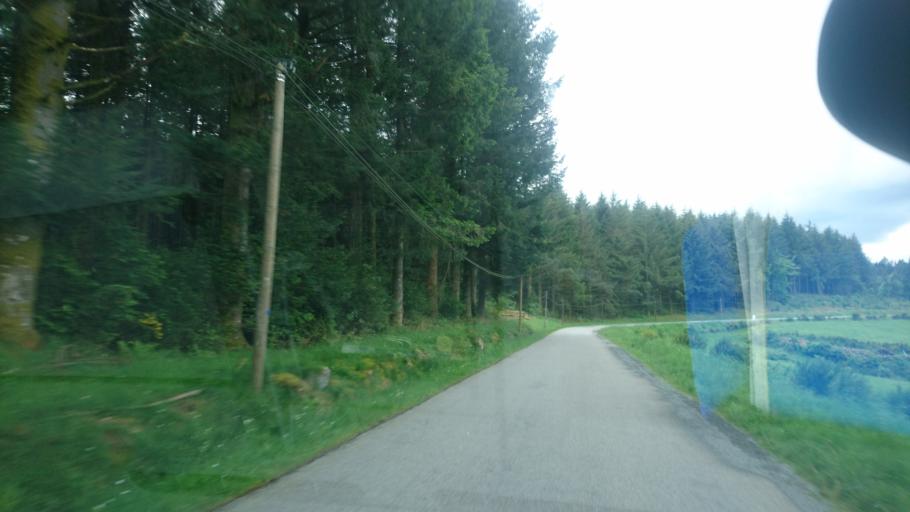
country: FR
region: Limousin
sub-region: Departement de la Haute-Vienne
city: Peyrat-le-Chateau
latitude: 45.8395
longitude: 1.9016
